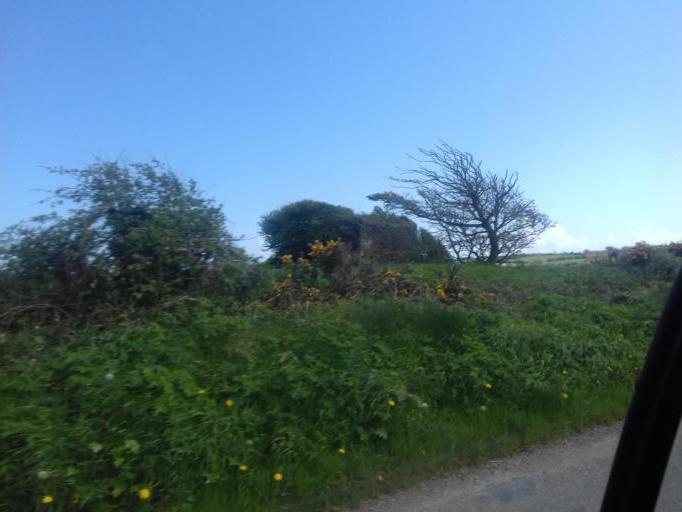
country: IE
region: Munster
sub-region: Waterford
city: Dunmore East
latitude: 52.1840
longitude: -6.8945
